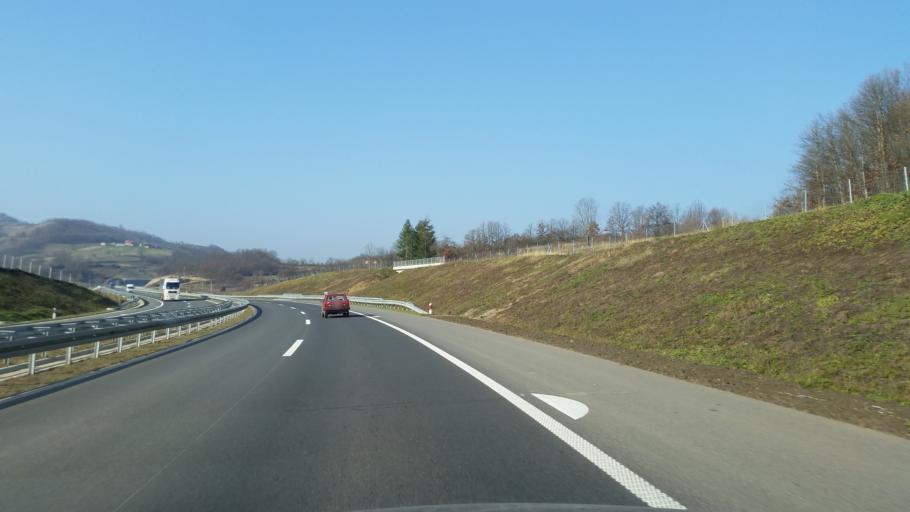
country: RS
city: Prislonica
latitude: 44.0002
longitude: 20.4020
